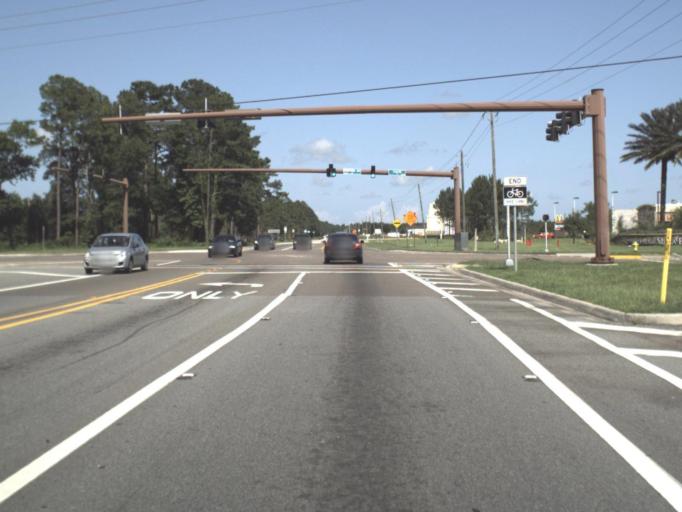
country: US
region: Florida
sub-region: Clay County
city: Green Cove Springs
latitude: 29.9635
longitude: -81.4922
